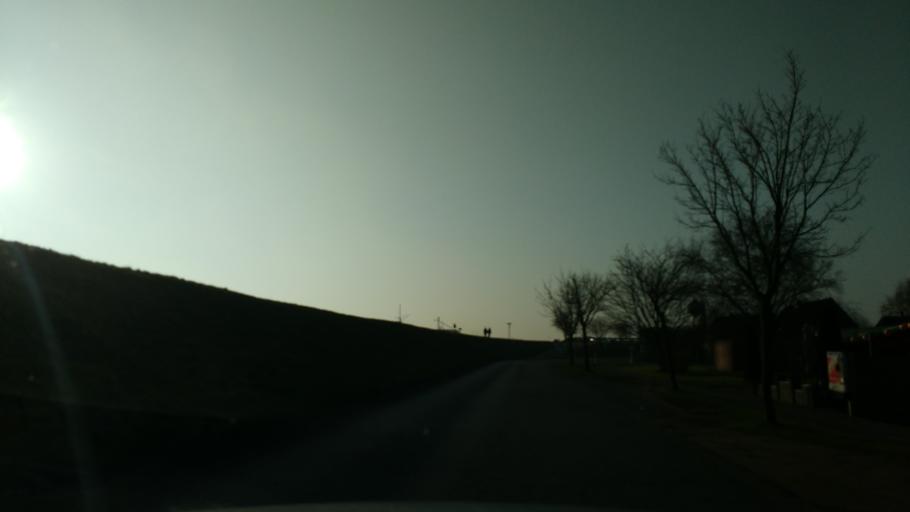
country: DE
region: Schleswig-Holstein
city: Friedrichskoog
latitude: 54.0025
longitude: 8.8800
